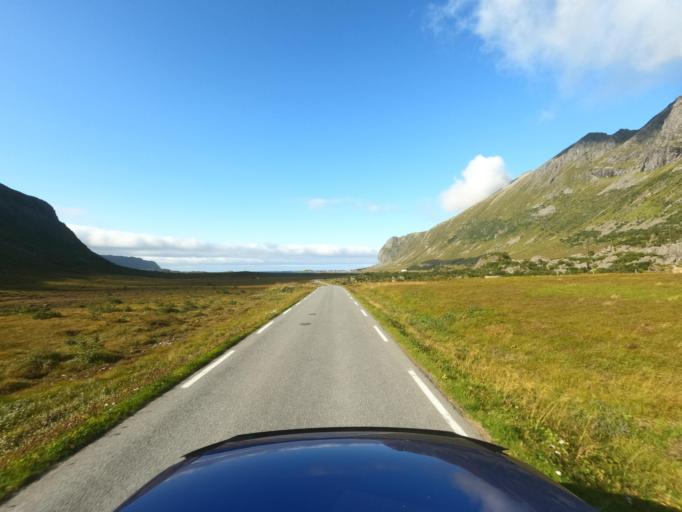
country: NO
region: Nordland
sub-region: Flakstad
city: Ramberg
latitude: 68.0662
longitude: 13.2375
